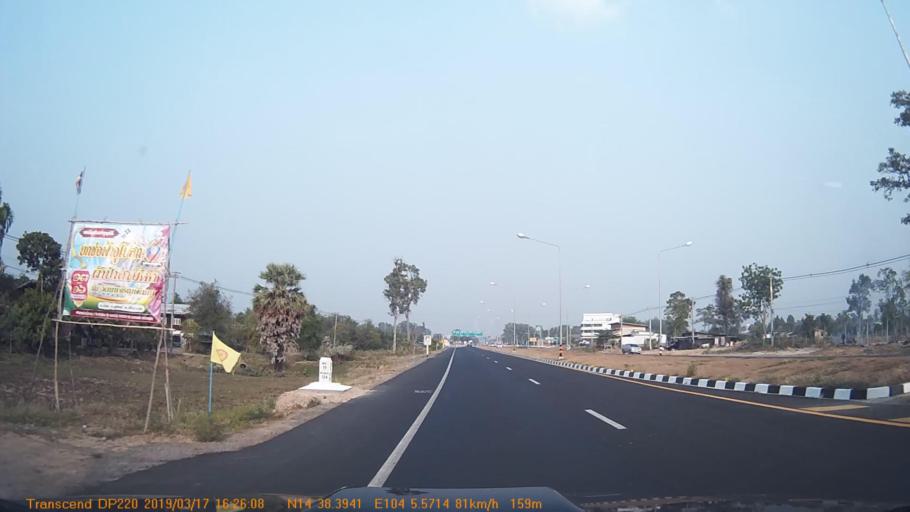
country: TH
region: Sisaket
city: Phu Sing
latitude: 14.6399
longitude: 104.0932
